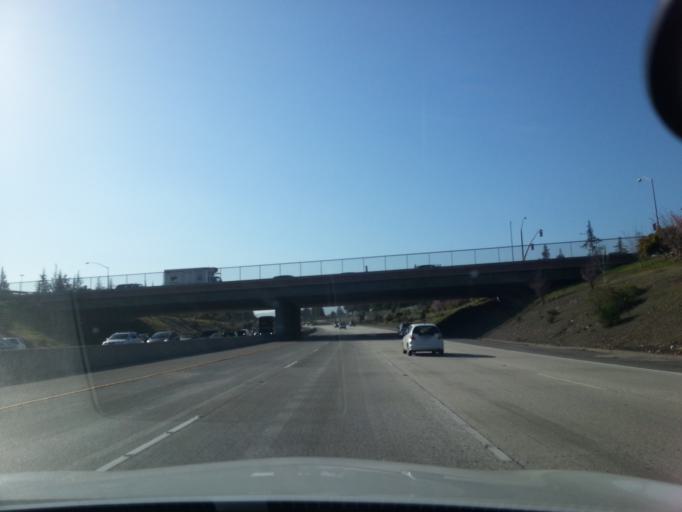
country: US
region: California
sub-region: Santa Clara County
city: Cupertino
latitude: 37.3237
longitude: -122.0503
